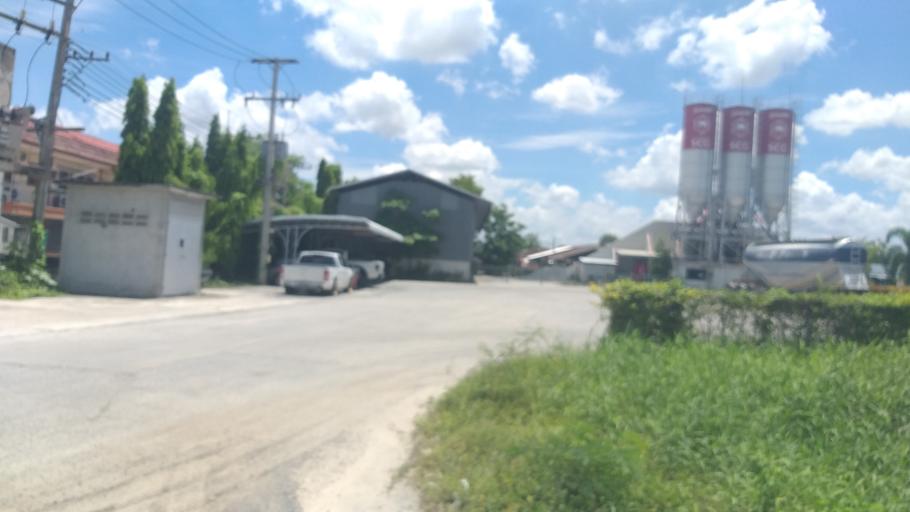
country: TH
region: Nakhon Nayok
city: Ban Na
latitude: 14.2683
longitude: 101.0656
